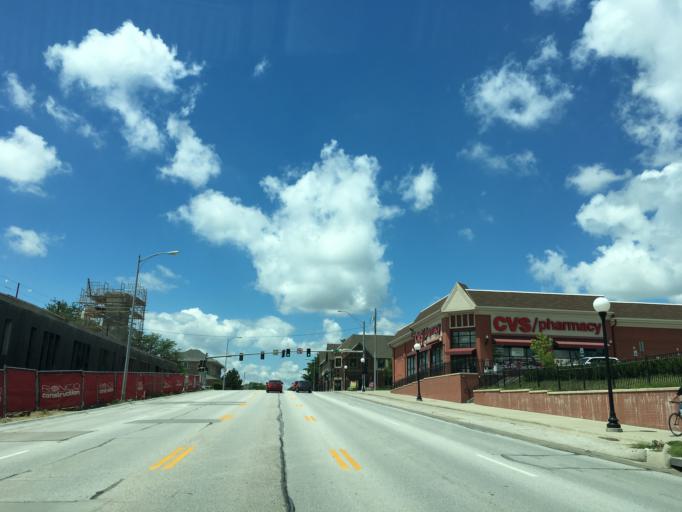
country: US
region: Nebraska
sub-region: Douglas County
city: Omaha
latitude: 41.2597
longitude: -95.9866
